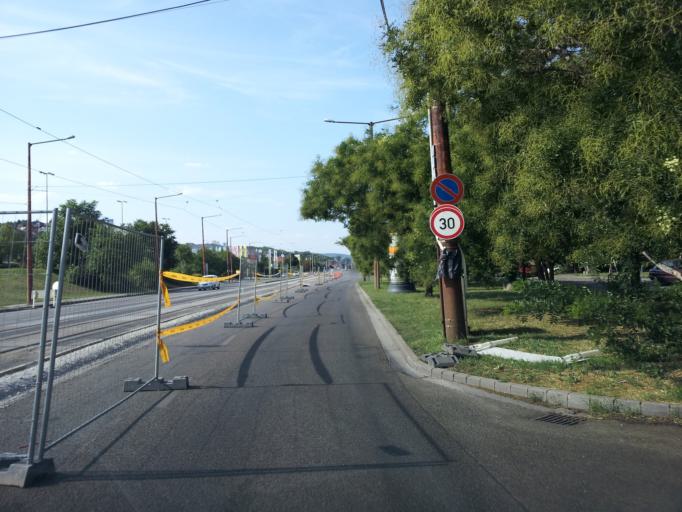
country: HU
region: Budapest
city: Budapest III. keruelet
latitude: 47.5415
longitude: 19.0306
